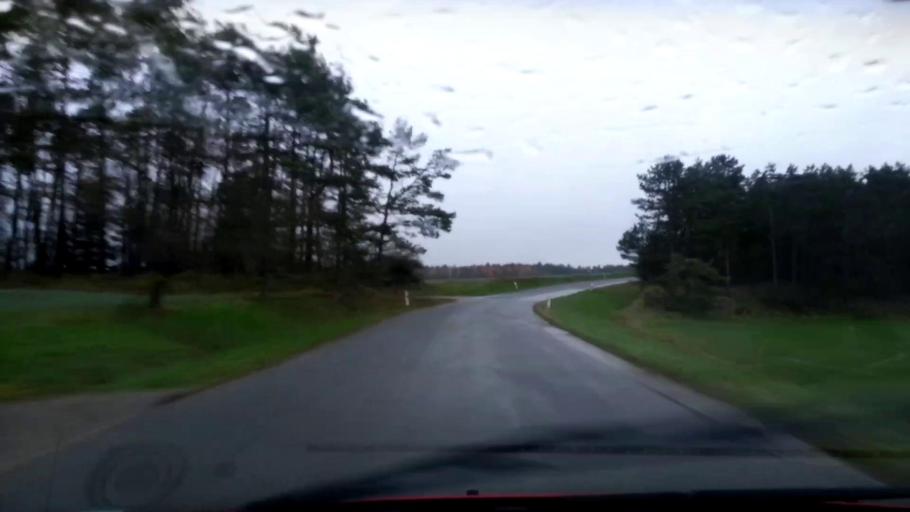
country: DE
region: Bavaria
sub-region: Upper Franconia
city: Aufsess
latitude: 49.9347
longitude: 11.2033
